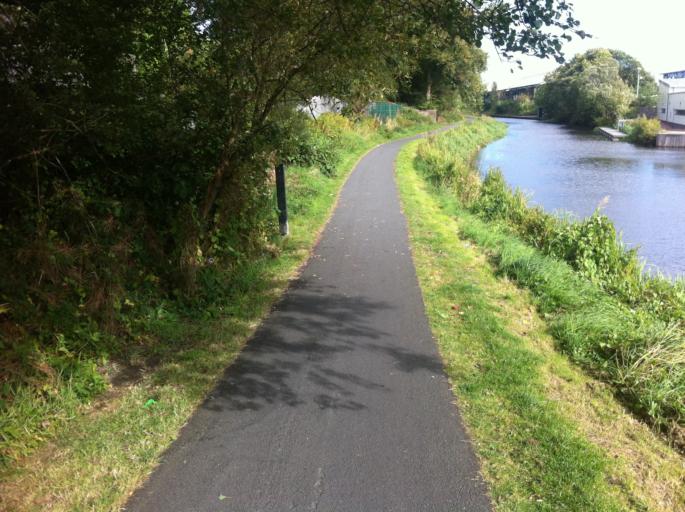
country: GB
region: Scotland
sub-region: East Dunbartonshire
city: Kirkintilloch
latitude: 55.9352
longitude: -4.1609
